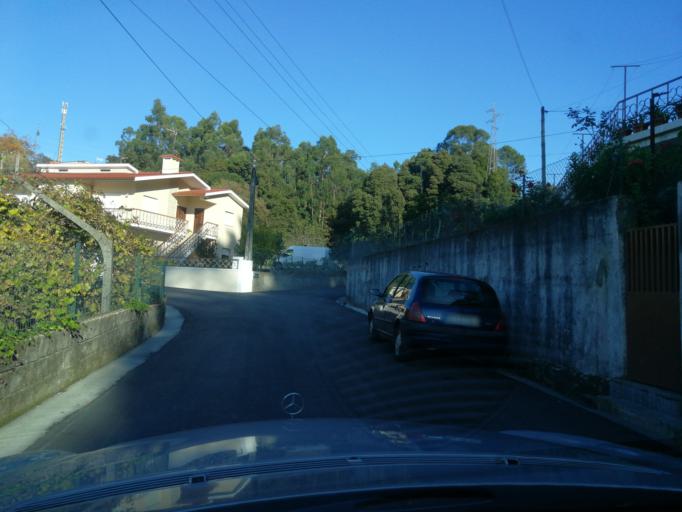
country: PT
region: Braga
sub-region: Vila Nova de Famalicao
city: Vila Nova de Famalicao
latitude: 41.4283
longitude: -8.5174
